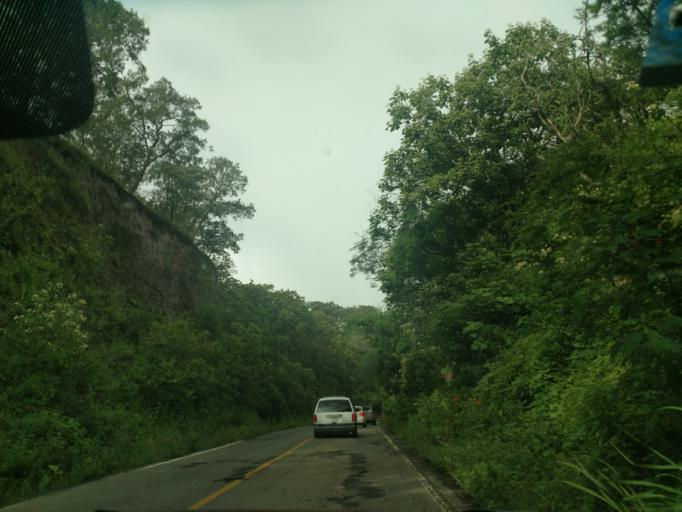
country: MX
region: Jalisco
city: El Salto
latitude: 20.4625
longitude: -104.3884
